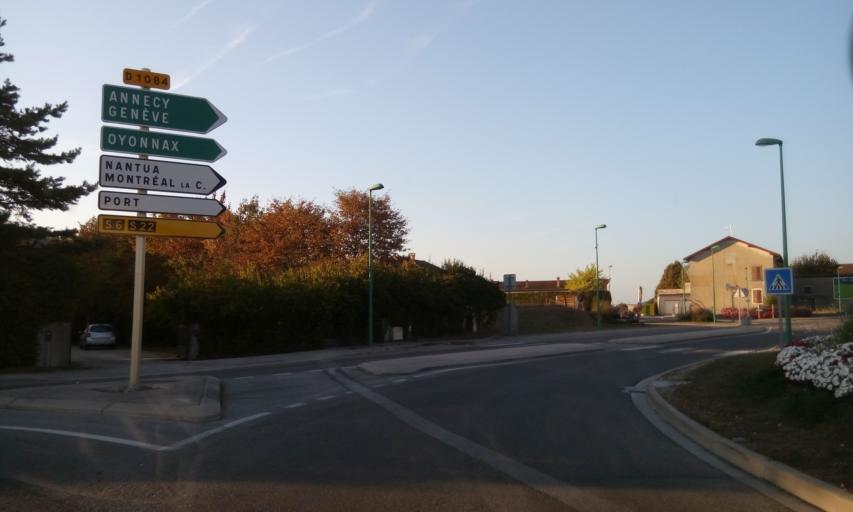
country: FR
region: Rhone-Alpes
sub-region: Departement de l'Ain
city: Saint-Martin-du-Frene
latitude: 46.1342
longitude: 5.5496
